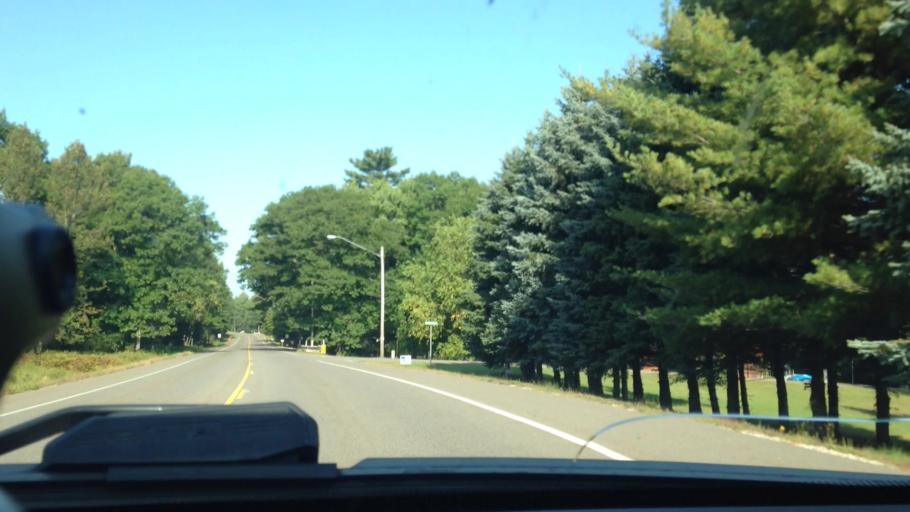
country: US
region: Michigan
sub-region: Dickinson County
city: Quinnesec
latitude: 45.8289
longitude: -87.9947
